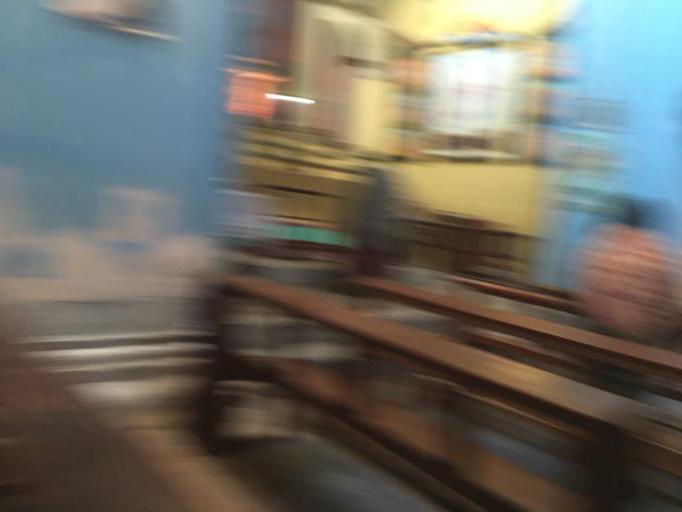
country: PE
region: Puno
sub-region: Provincia de Chucuito
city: Kelluyo
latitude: -17.0660
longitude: -69.1930
